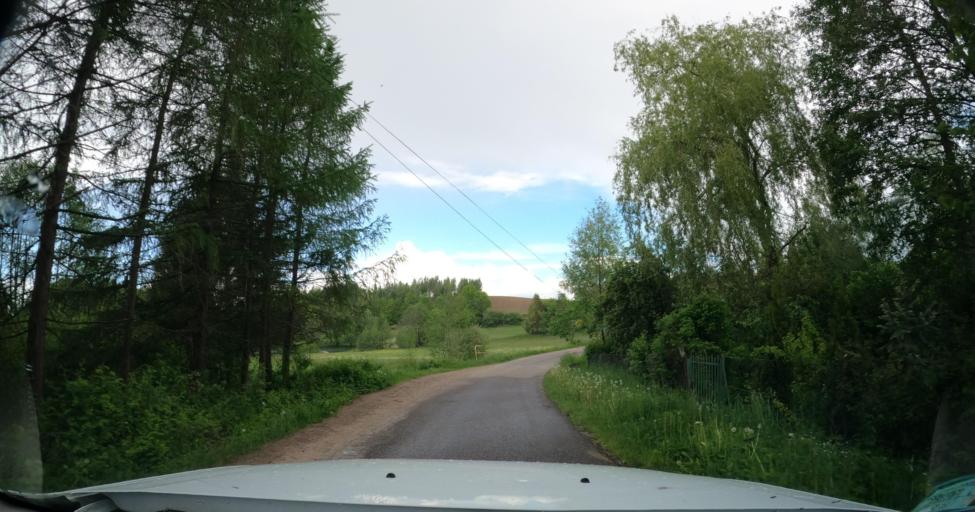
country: PL
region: Pomeranian Voivodeship
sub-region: Powiat kartuski
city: Garcz
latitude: 54.3351
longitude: 18.1381
